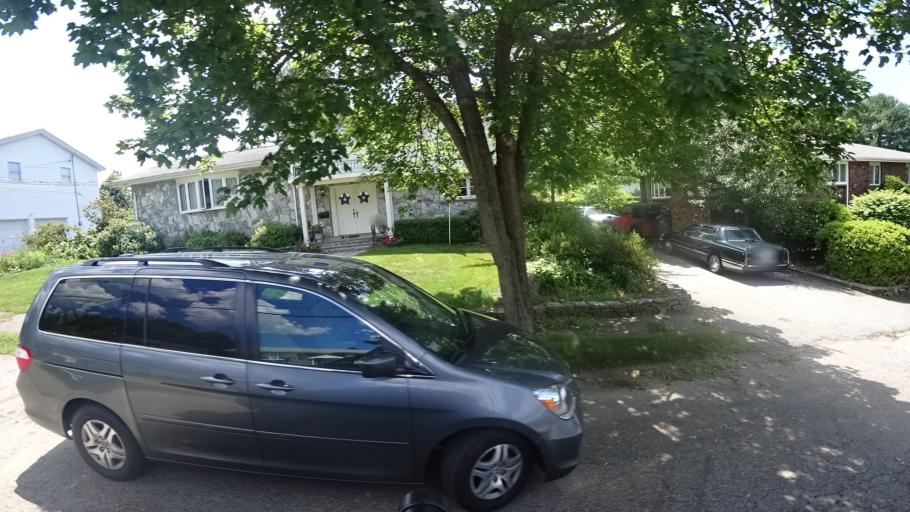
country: US
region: Massachusetts
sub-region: Norfolk County
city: Dedham
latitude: 42.2710
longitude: -71.1844
